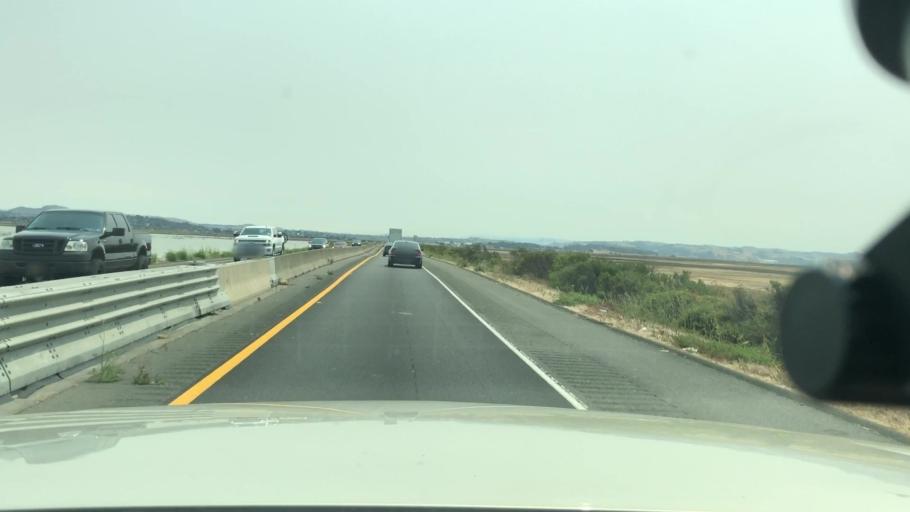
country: US
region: California
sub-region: Solano County
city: Vallejo
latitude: 38.1263
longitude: -122.3231
